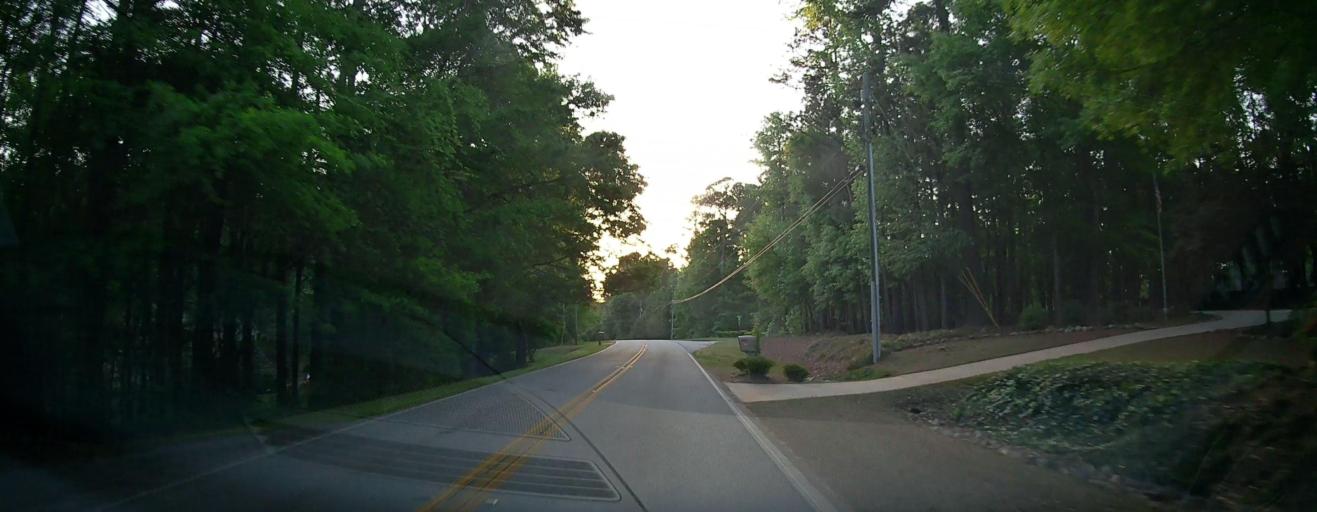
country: US
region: Georgia
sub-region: Henry County
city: McDonough
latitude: 33.4061
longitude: -84.1052
